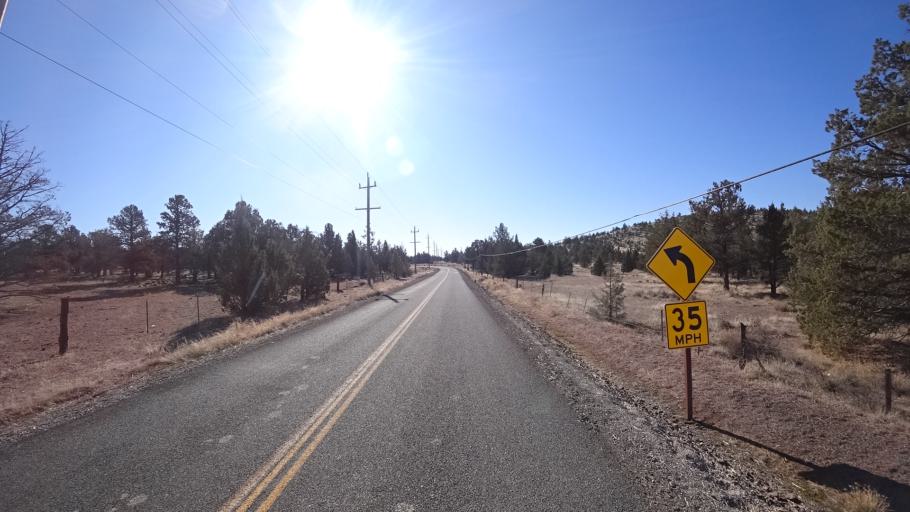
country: US
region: California
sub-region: Siskiyou County
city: Montague
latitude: 41.6644
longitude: -122.3690
